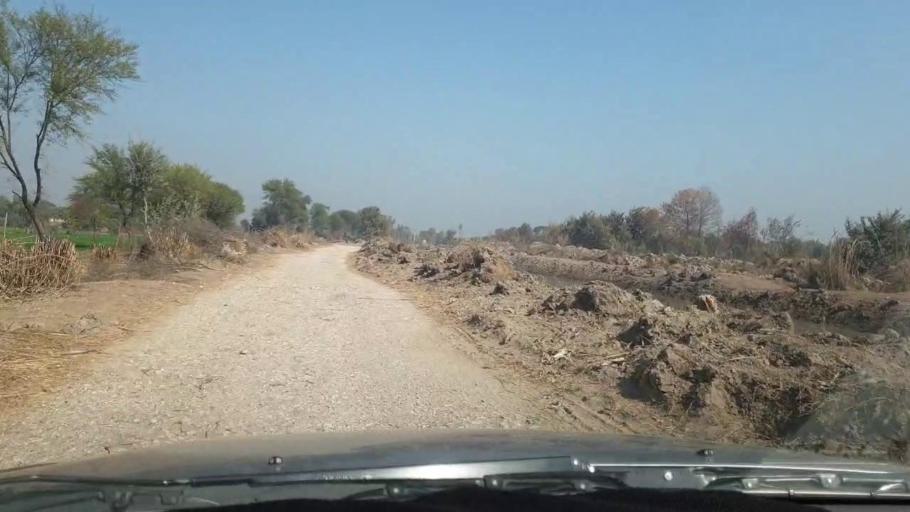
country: PK
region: Sindh
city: Khanpur
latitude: 27.7751
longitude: 69.5372
